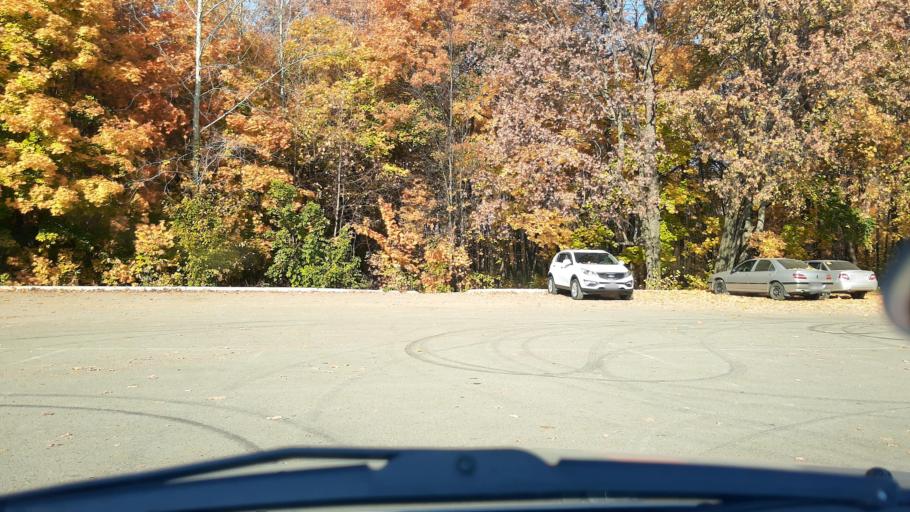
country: RU
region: Bashkortostan
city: Ufa
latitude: 54.7305
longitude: 56.0106
